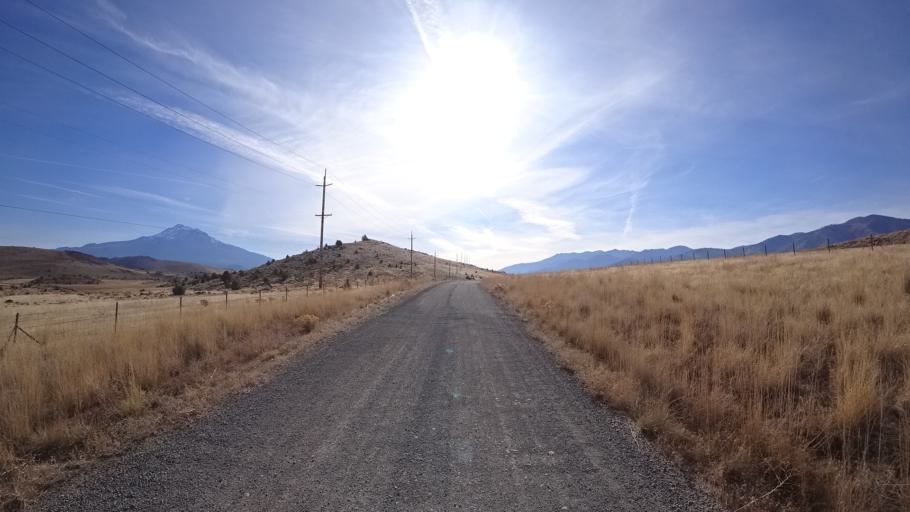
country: US
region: California
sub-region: Siskiyou County
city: Weed
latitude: 41.5215
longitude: -122.4739
